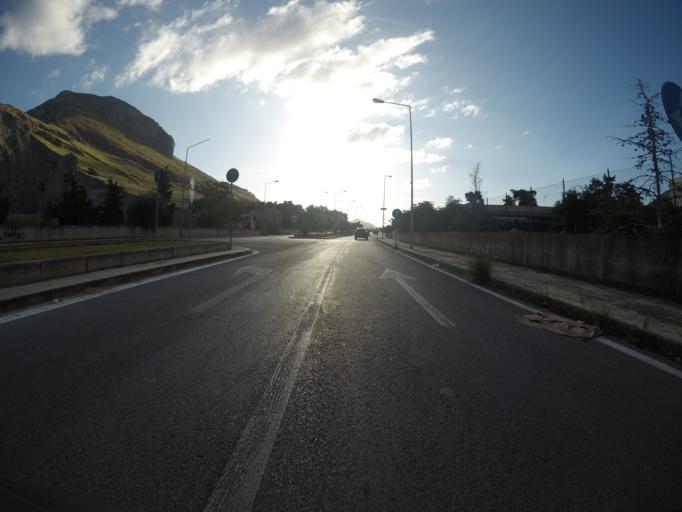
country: IT
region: Sicily
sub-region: Palermo
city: Isola delle Femmine
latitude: 38.1947
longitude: 13.2831
